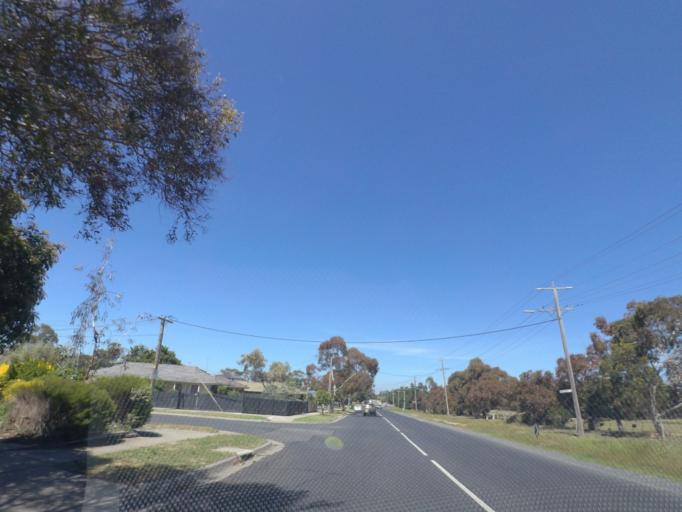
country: AU
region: Victoria
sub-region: Hume
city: Sunbury
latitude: -37.5788
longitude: 144.6933
